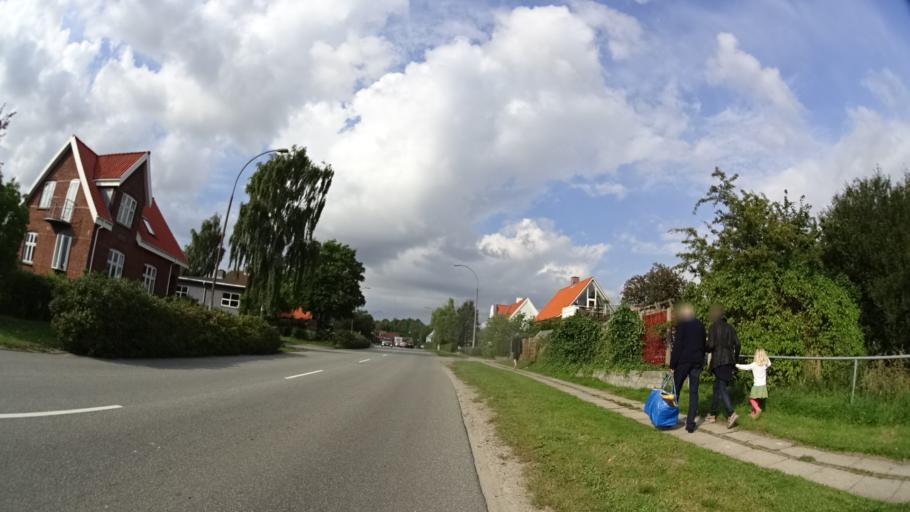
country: DK
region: Central Jutland
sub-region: Arhus Kommune
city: Stavtrup
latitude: 56.1516
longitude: 10.0906
